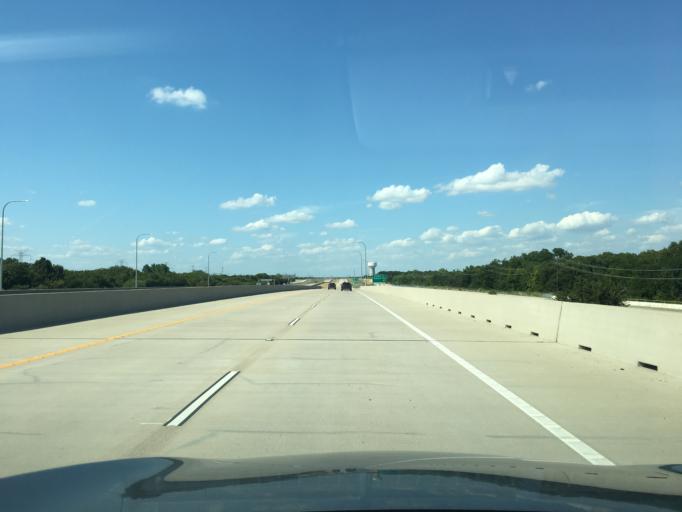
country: US
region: Texas
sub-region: Tarrant County
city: Mansfield
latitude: 32.5893
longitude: -97.0778
